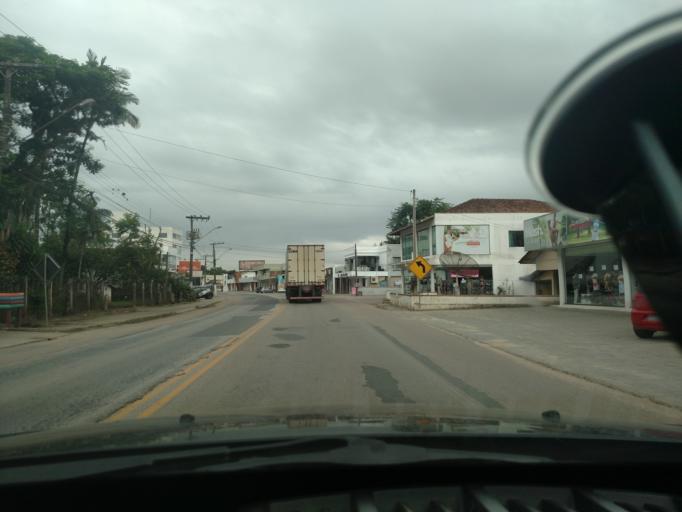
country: BR
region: Santa Catarina
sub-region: Gaspar
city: Gaspar
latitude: -26.9040
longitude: -48.8352
